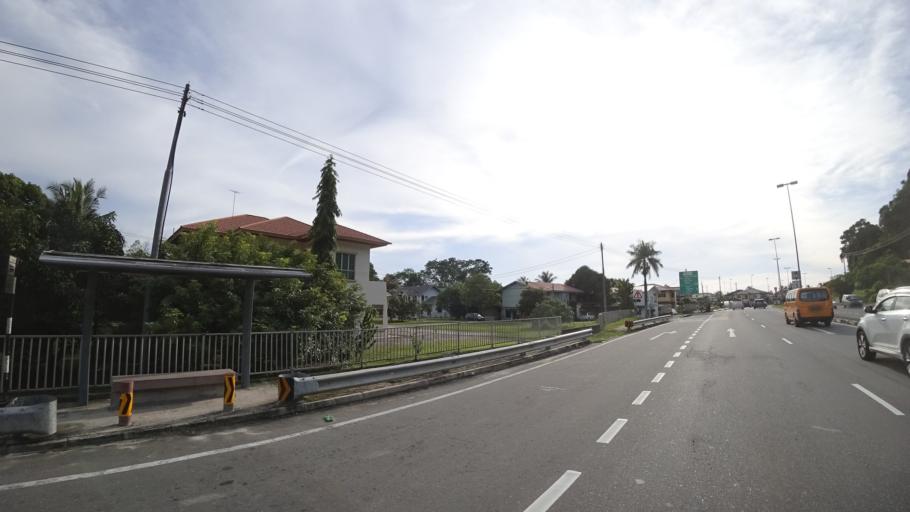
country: BN
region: Brunei and Muara
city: Bandar Seri Begawan
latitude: 4.8523
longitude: 114.8777
